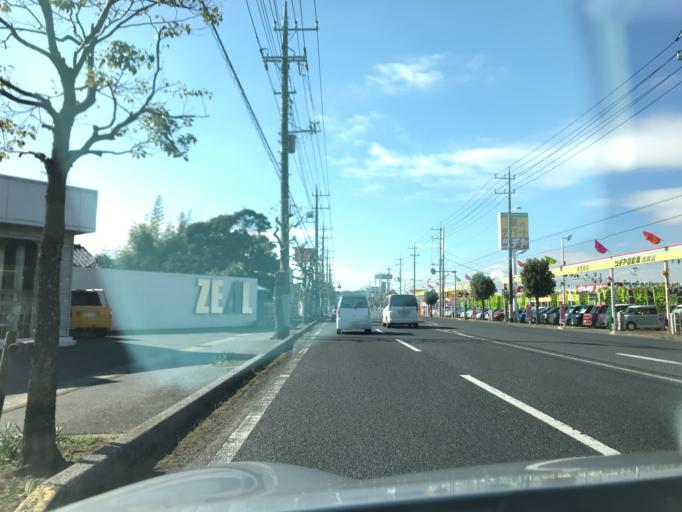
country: JP
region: Chiba
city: Mobara
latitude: 35.4430
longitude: 140.2922
